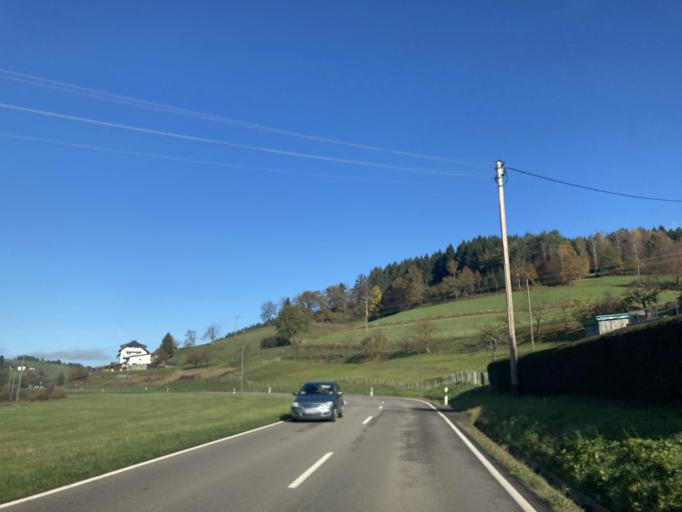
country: DE
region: Baden-Wuerttemberg
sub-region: Freiburg Region
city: Elzach
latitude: 48.1887
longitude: 8.0858
